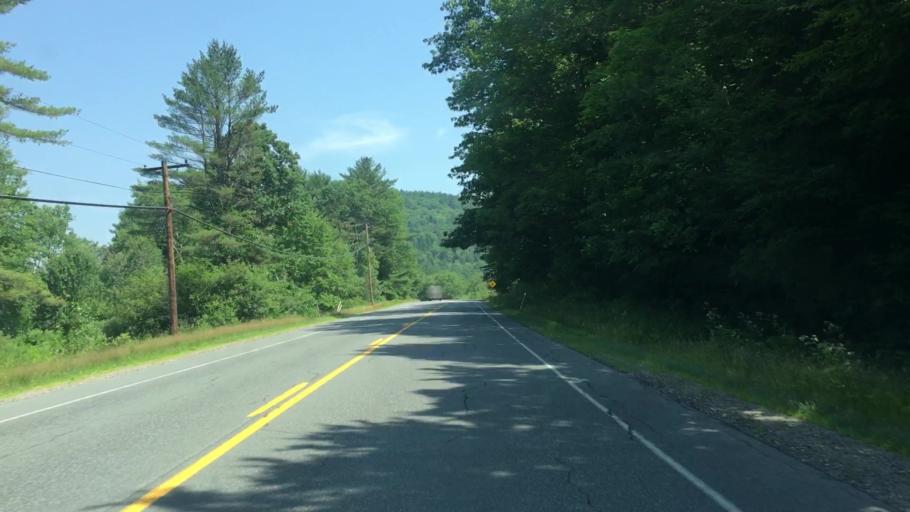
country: US
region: New Hampshire
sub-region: Sullivan County
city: Grantham
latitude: 43.4600
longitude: -72.1489
